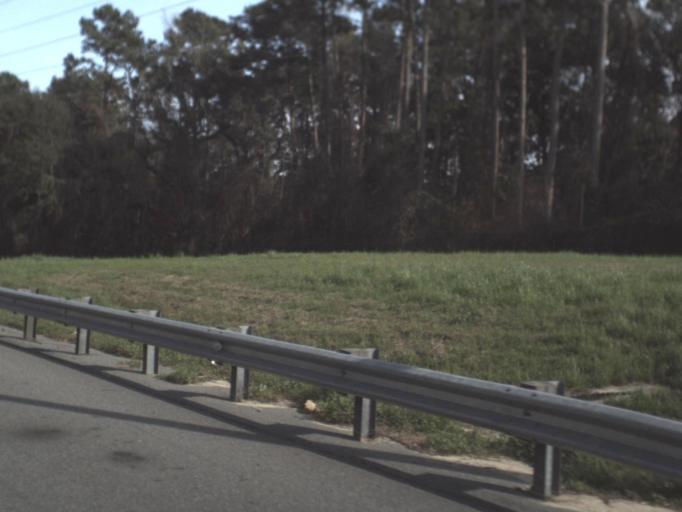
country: US
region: Florida
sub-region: Leon County
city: Tallahassee
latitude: 30.4785
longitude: -84.3272
